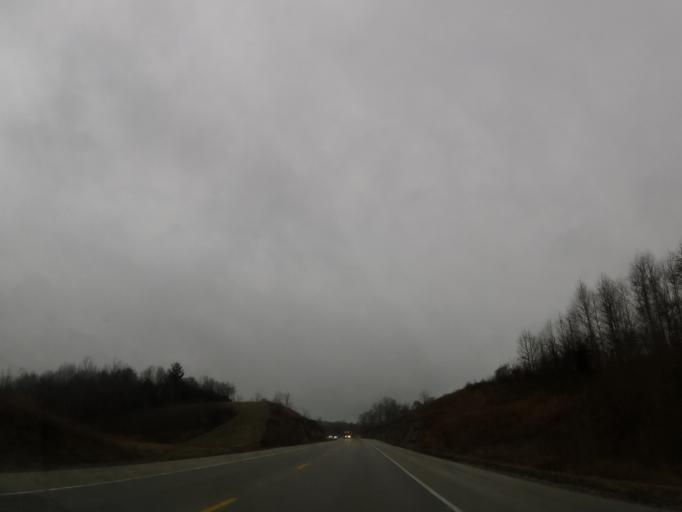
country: US
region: Kentucky
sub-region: Rockcastle County
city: Brodhead
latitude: 37.3662
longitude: -84.4112
